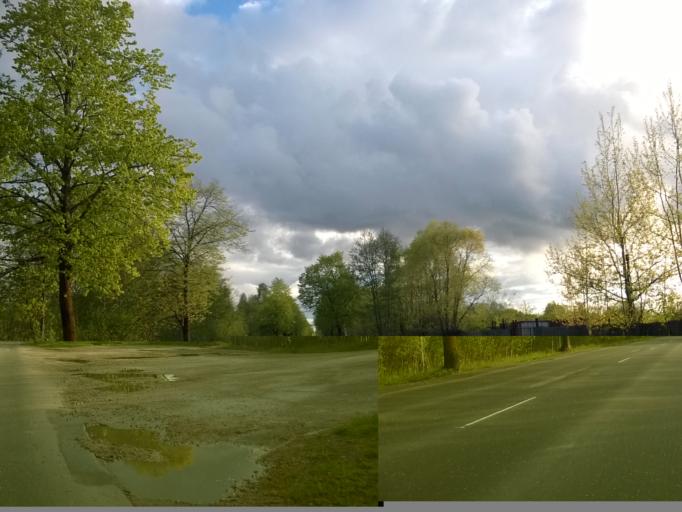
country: LV
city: Tireli
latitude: 56.9361
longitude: 23.5954
